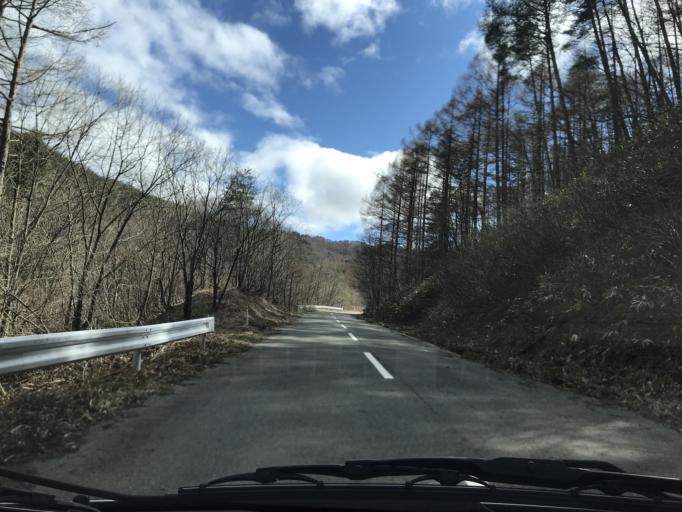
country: JP
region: Iwate
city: Mizusawa
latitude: 39.0636
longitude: 140.9719
